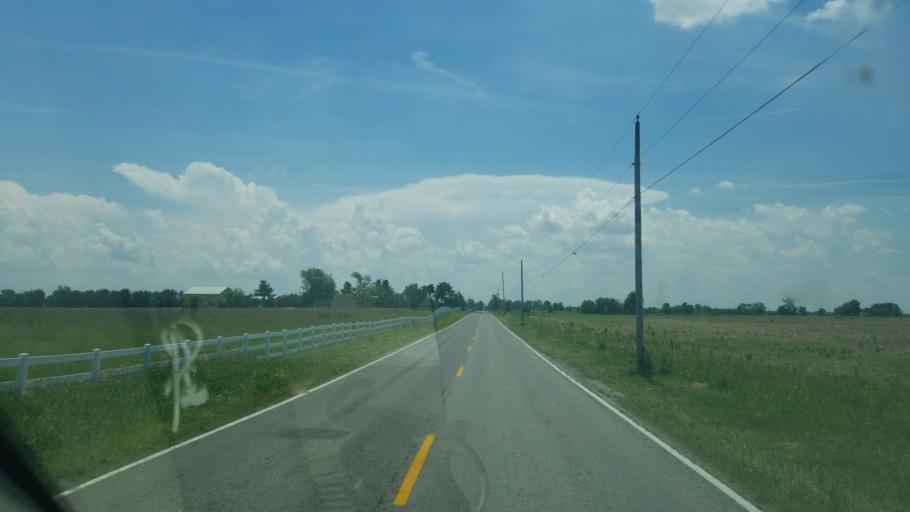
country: US
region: Ohio
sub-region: Hancock County
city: Arlington
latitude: 40.9467
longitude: -83.5943
